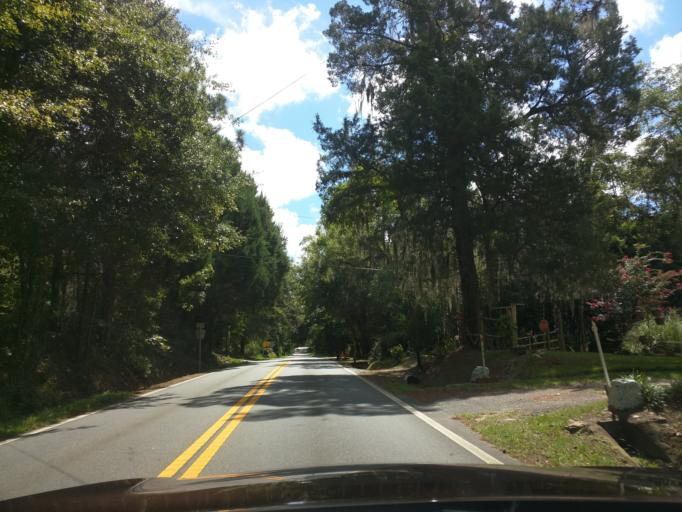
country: US
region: Florida
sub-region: Gadsden County
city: Havana
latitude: 30.5873
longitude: -84.2778
